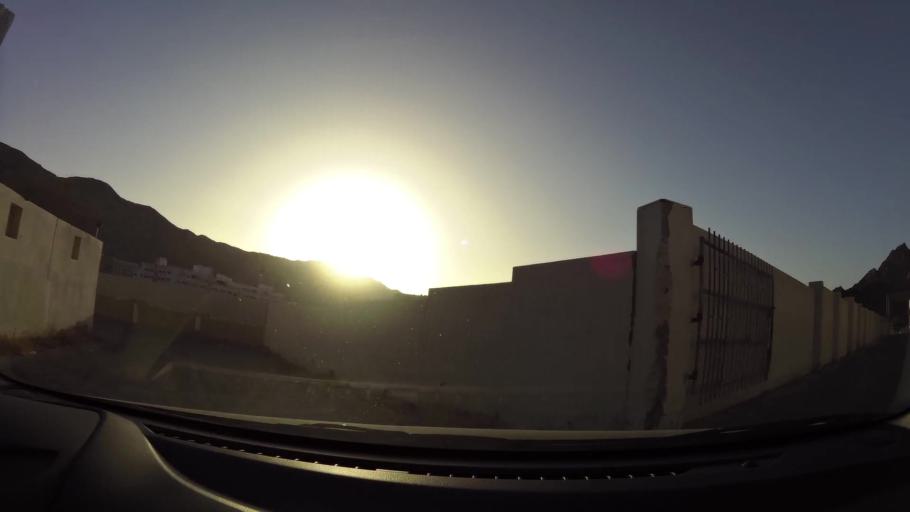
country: OM
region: Muhafazat Masqat
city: Muscat
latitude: 23.5700
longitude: 58.5758
